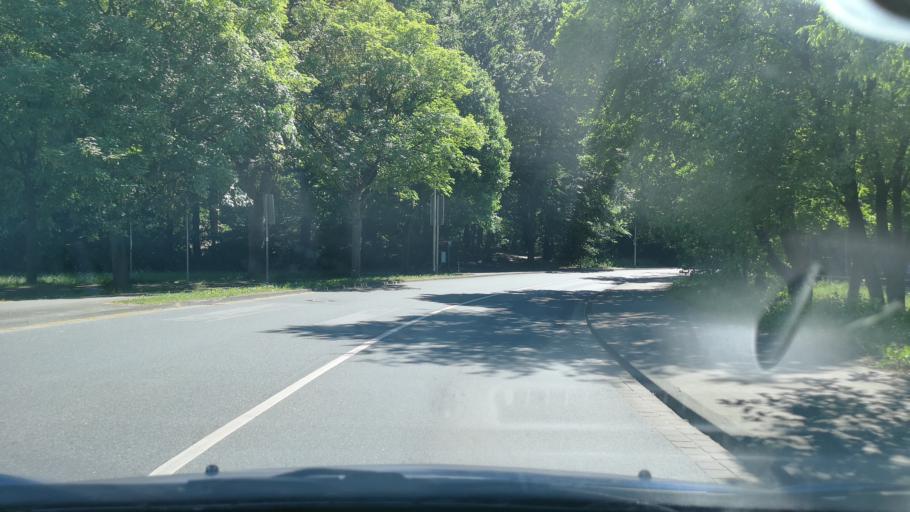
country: DE
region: Lower Saxony
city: Auf der Horst
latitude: 52.4109
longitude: 9.6321
